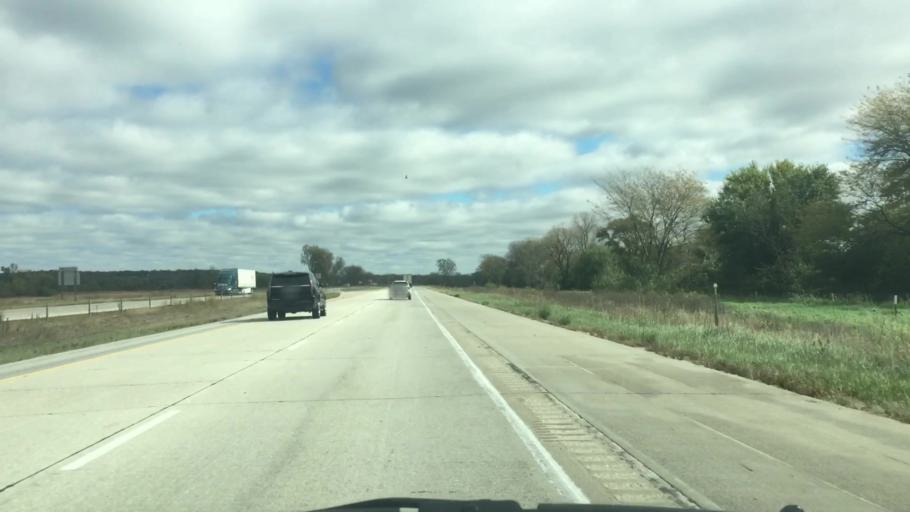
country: US
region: Iowa
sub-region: Polk County
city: Mitchellville
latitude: 41.6814
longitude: -93.3199
